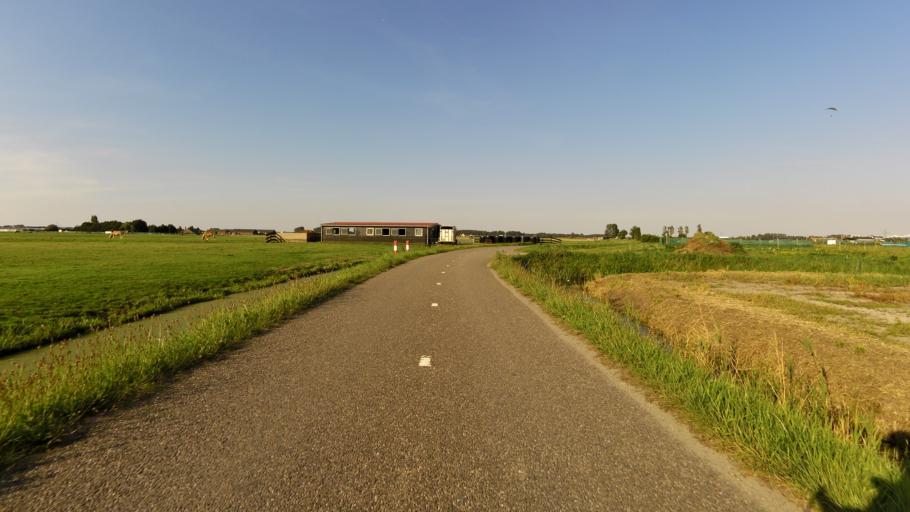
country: NL
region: South Holland
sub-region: Gemeente Oegstgeest
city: Oegstgeest
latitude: 52.2030
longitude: 4.4621
